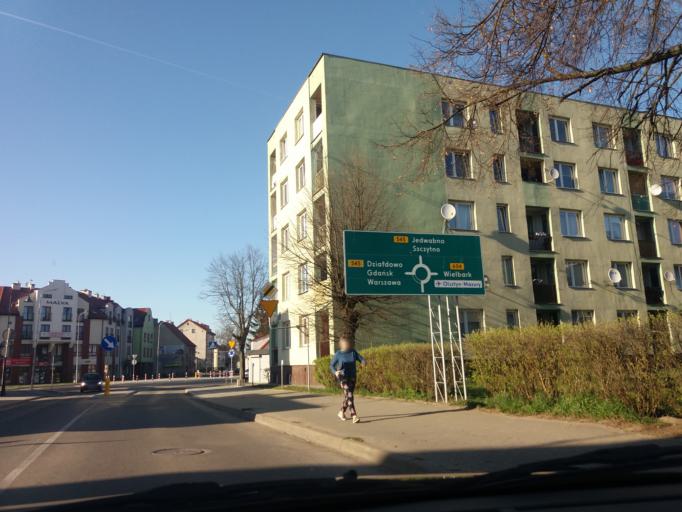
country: PL
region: Warmian-Masurian Voivodeship
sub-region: Powiat nidzicki
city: Nidzica
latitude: 53.3608
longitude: 20.4258
